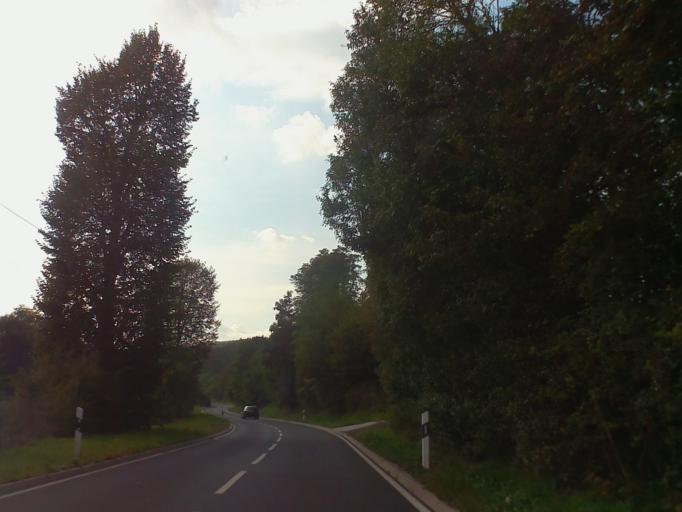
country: DE
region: Thuringia
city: Lauchroden
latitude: 51.0123
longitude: 10.1138
